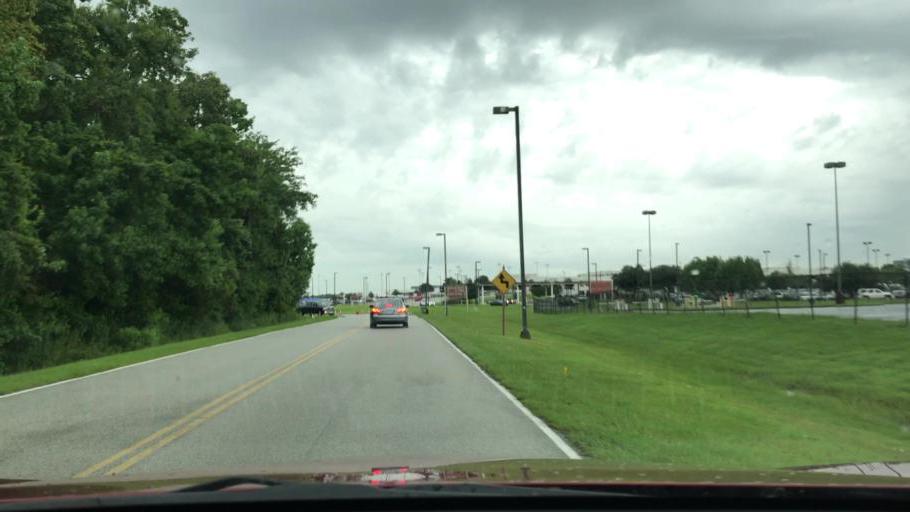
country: US
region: South Carolina
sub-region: Berkeley County
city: Hanahan
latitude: 32.8808
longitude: -80.0408
